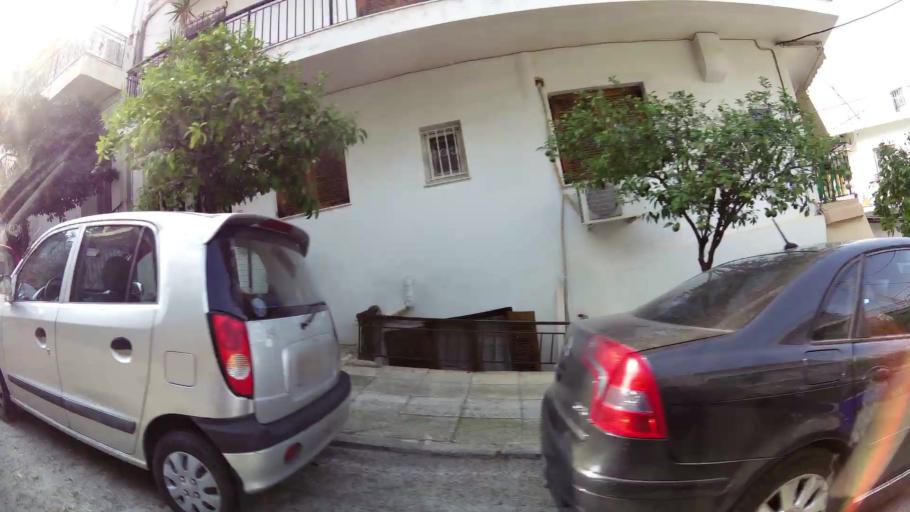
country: GR
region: Attica
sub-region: Nomarchia Athinas
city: Galatsi
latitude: 38.0070
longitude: 23.7532
